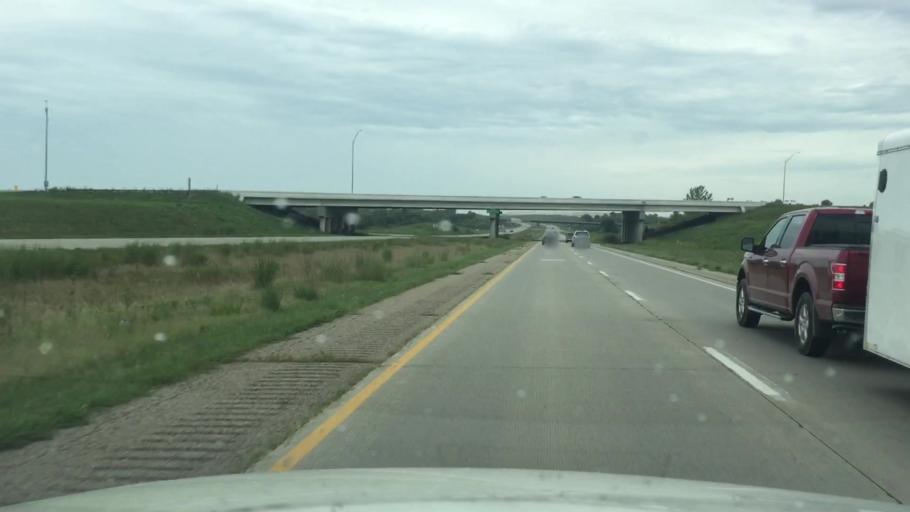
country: US
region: Iowa
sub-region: Warren County
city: Norwalk
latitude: 41.5068
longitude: -93.6430
